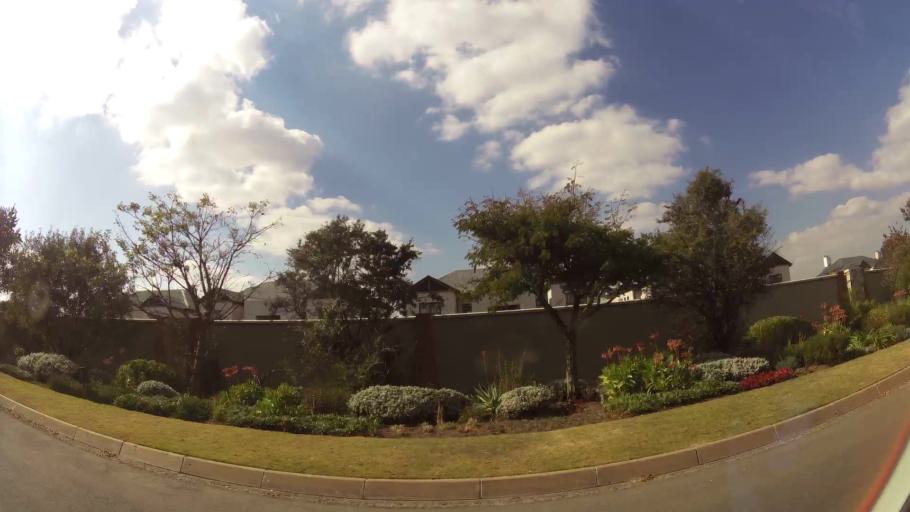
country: ZA
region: Gauteng
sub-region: City of Johannesburg Metropolitan Municipality
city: Midrand
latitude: -26.0254
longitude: 28.0838
